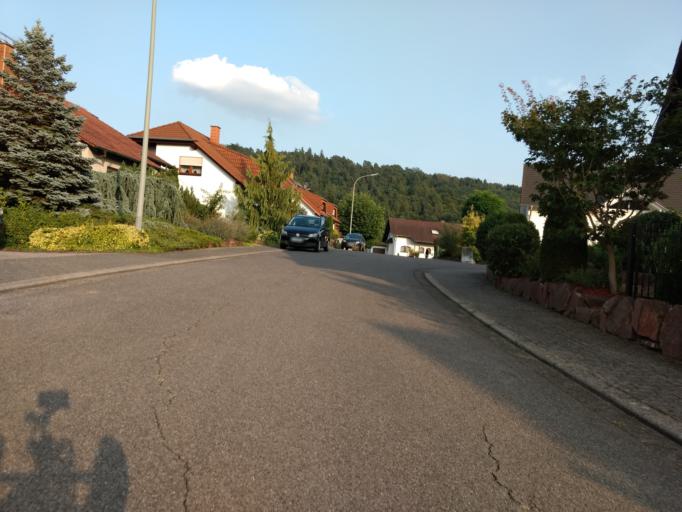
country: DE
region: Saarland
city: Rehlingen-Siersburg
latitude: 49.3595
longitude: 6.6700
